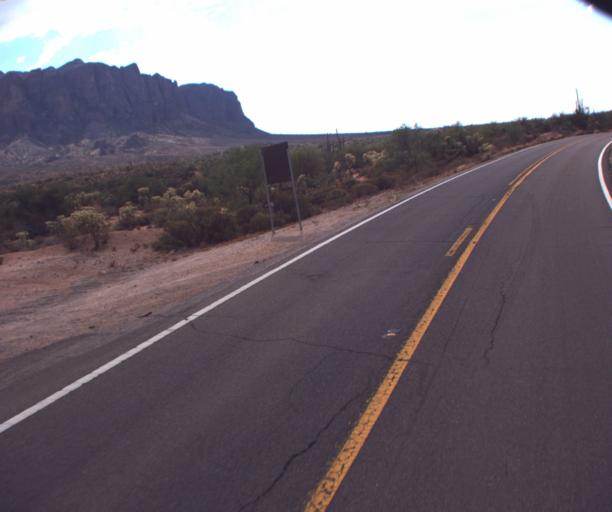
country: US
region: Arizona
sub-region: Pinal County
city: Apache Junction
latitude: 33.4737
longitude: -111.4755
